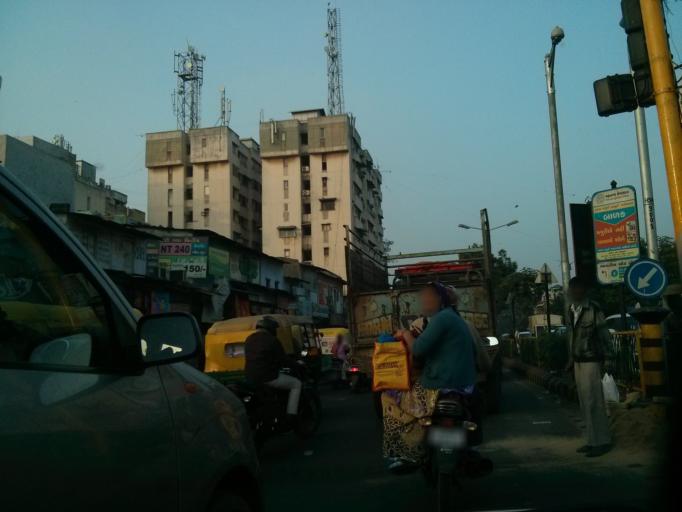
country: IN
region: Gujarat
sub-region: Ahmadabad
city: Ahmedabad
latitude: 23.0382
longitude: 72.5880
